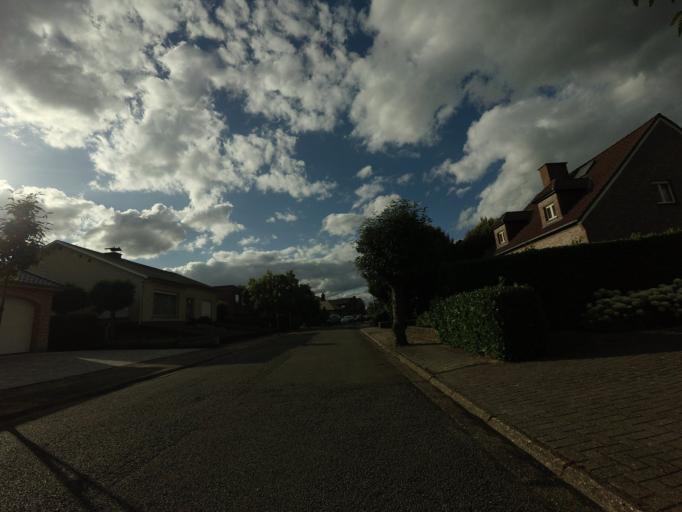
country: BE
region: Flanders
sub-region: Provincie Vlaams-Brabant
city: Kapelle-op-den-Bos
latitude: 51.0012
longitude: 4.3577
